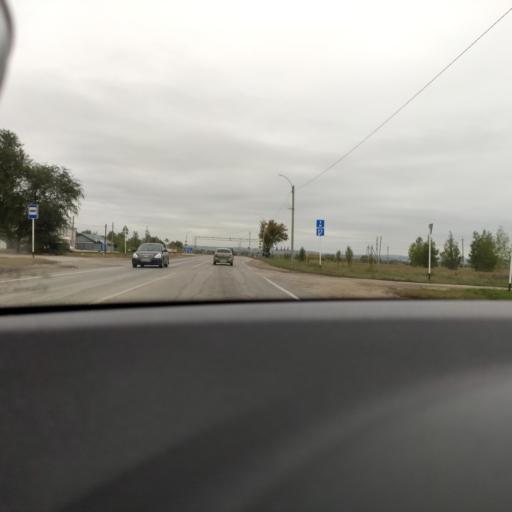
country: RU
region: Samara
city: Krasnyy Yar
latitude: 53.4808
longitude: 50.3922
